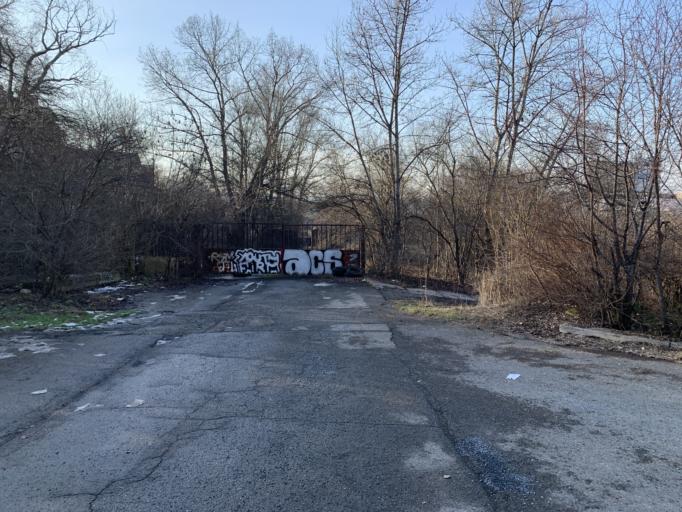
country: CZ
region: Praha
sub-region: Praha 8
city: Liben
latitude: 50.0583
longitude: 14.4886
